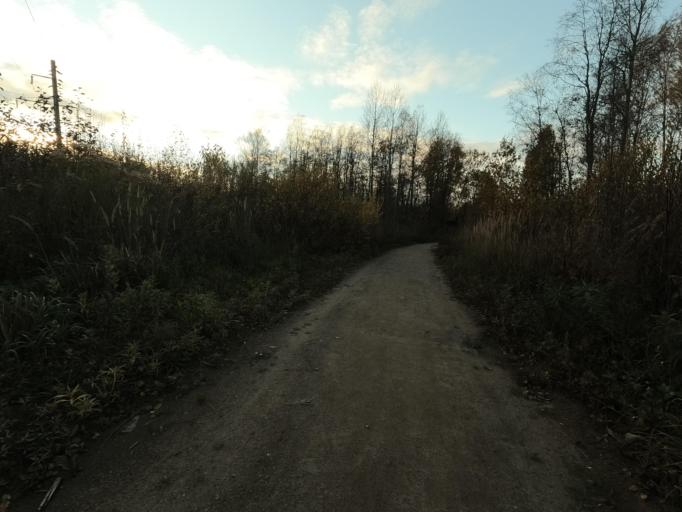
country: RU
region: Leningrad
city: Mga
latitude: 59.7746
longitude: 31.2245
